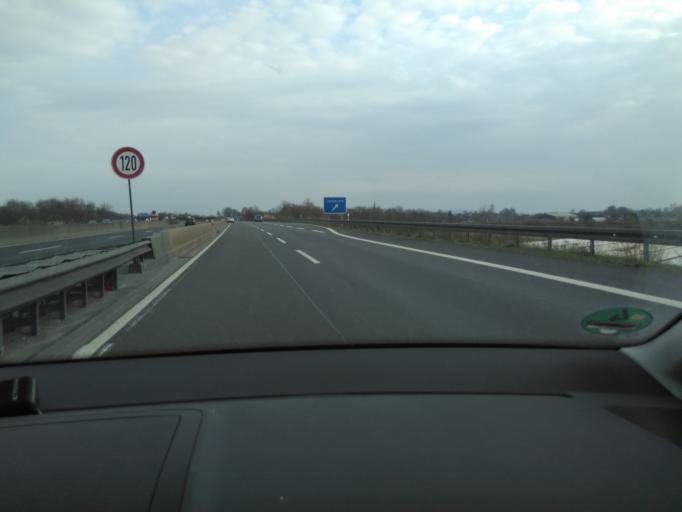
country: DE
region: North Rhine-Westphalia
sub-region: Regierungsbezirk Koln
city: Titz
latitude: 51.0444
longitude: 6.4521
